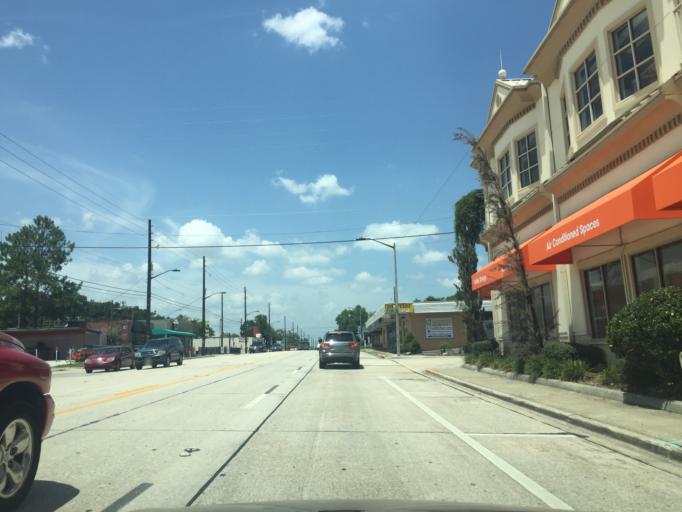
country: US
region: Florida
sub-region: Orange County
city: Orlando
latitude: 28.5591
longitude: -81.3644
